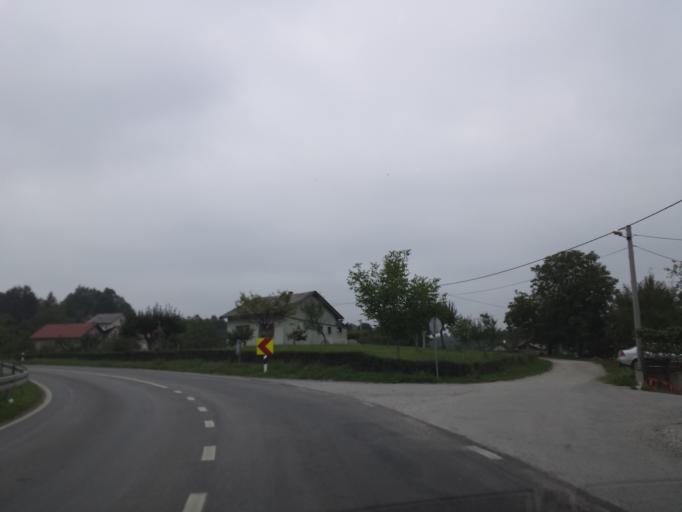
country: HR
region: Karlovacka
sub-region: Grad Karlovac
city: Karlovac
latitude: 45.4055
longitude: 15.4456
